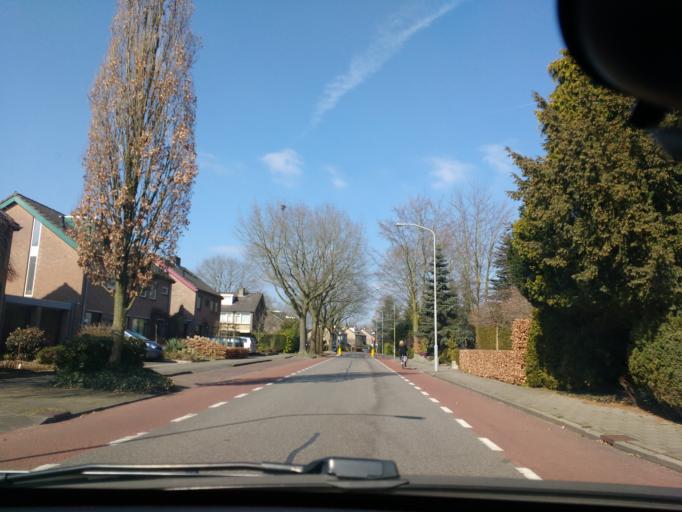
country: NL
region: Gelderland
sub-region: Gemeente Nijmegen
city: Nijmegen
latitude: 51.7866
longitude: 5.8574
